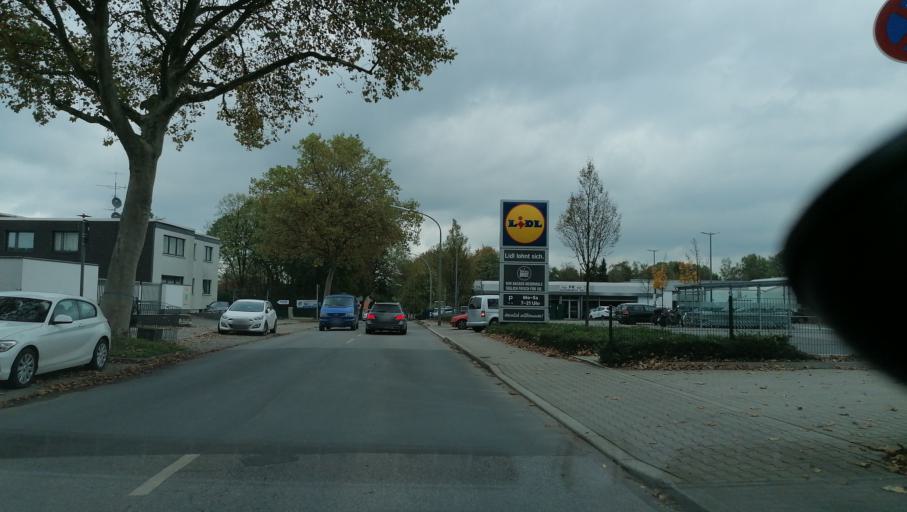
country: DE
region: North Rhine-Westphalia
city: Herten
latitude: 51.5755
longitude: 7.1171
